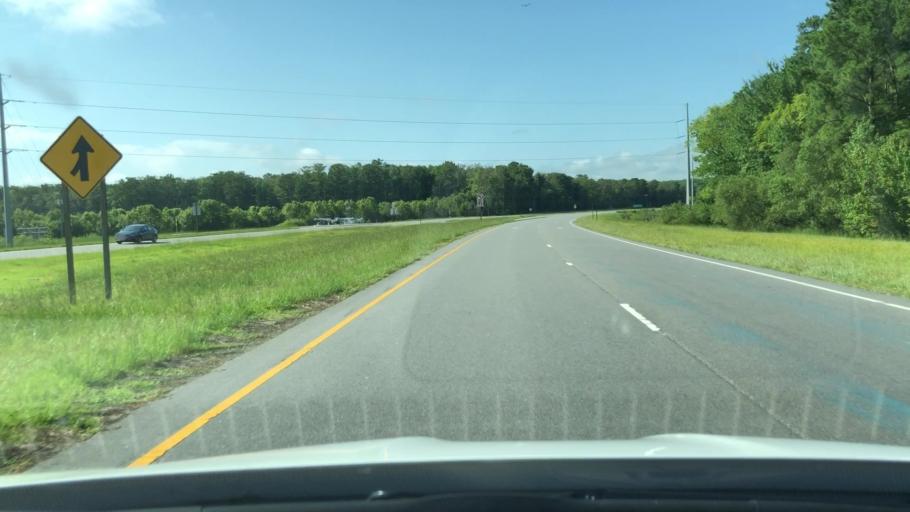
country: US
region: North Carolina
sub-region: Pasquotank County
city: Elizabeth City
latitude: 36.4373
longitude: -76.3388
